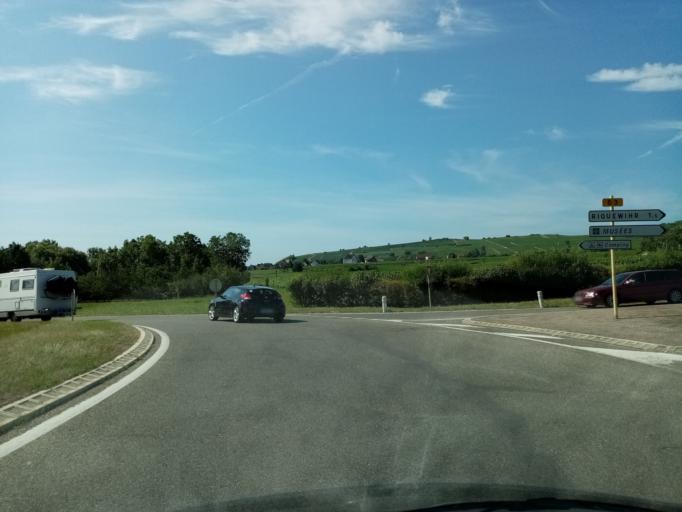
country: FR
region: Alsace
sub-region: Departement du Haut-Rhin
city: Bennwihr
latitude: 48.1596
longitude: 7.3182
